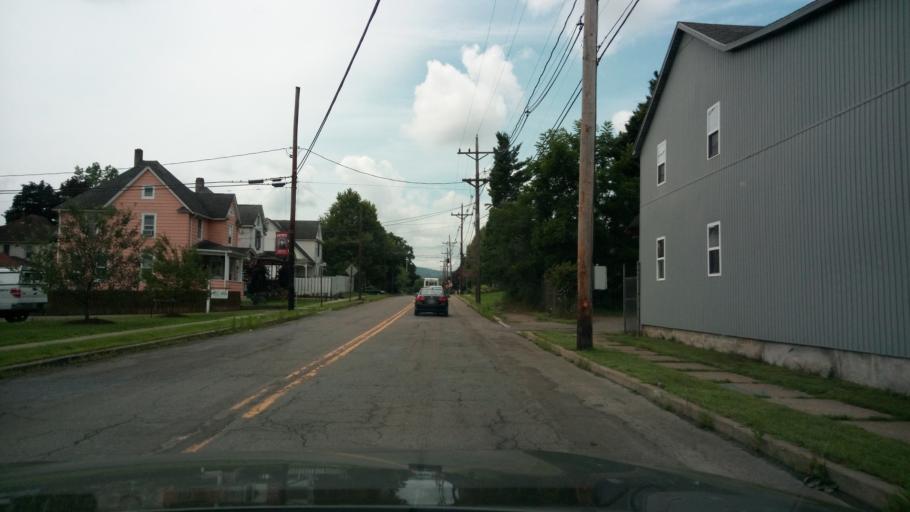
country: US
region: Pennsylvania
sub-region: Bradford County
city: Sayre
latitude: 41.9910
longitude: -76.5225
